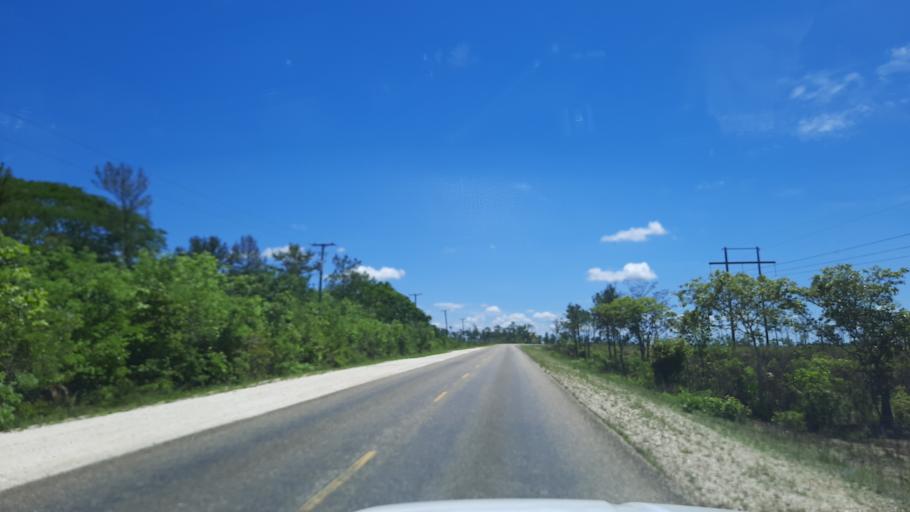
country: BZ
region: Cayo
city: Belmopan
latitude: 17.3524
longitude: -88.5518
